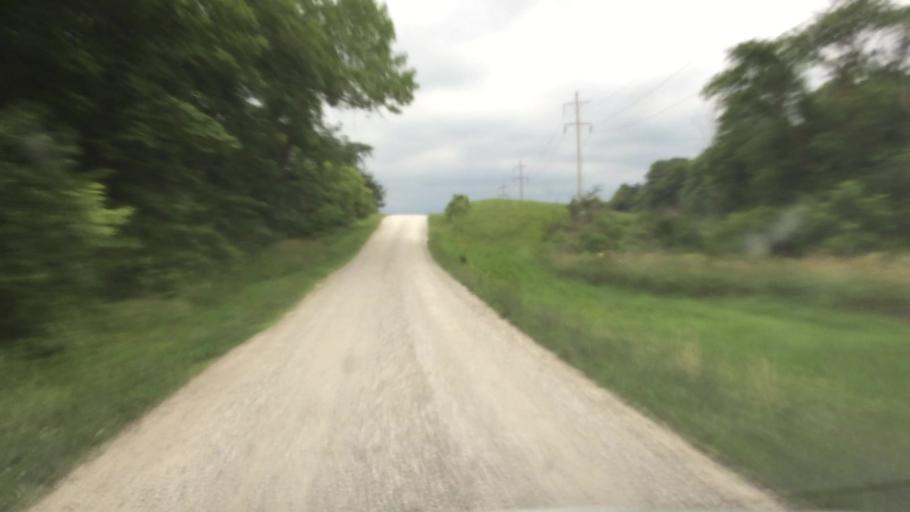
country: US
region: Illinois
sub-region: Adams County
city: Camp Point
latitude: 40.2156
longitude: -90.9544
